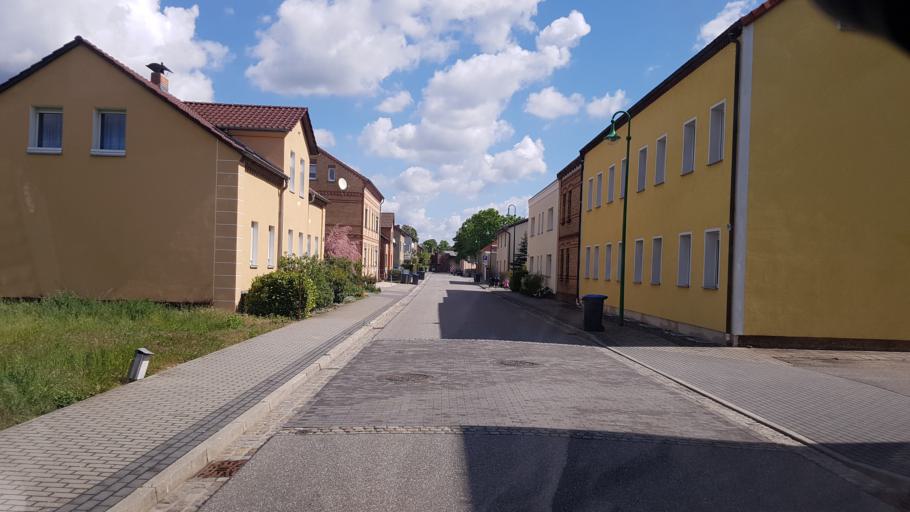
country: DE
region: Brandenburg
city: Grossraschen
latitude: 51.5826
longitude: 14.0038
